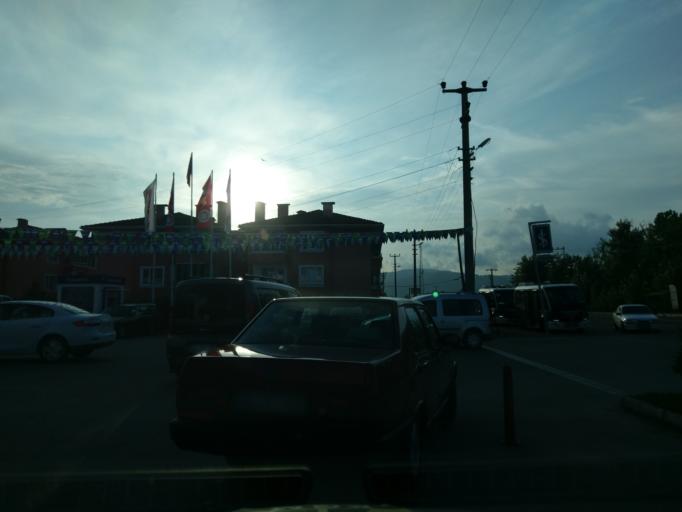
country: TR
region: Ordu
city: Ordu
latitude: 41.0192
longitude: 37.8332
